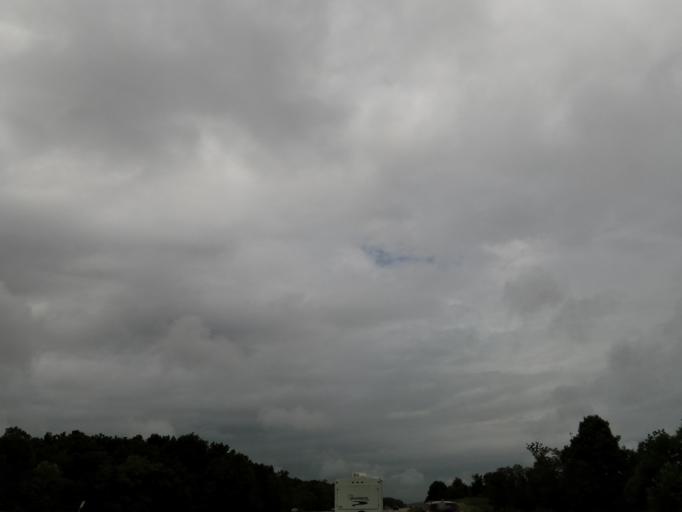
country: US
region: Illinois
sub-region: Clinton County
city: Wamac
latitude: 38.3644
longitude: -89.0848
